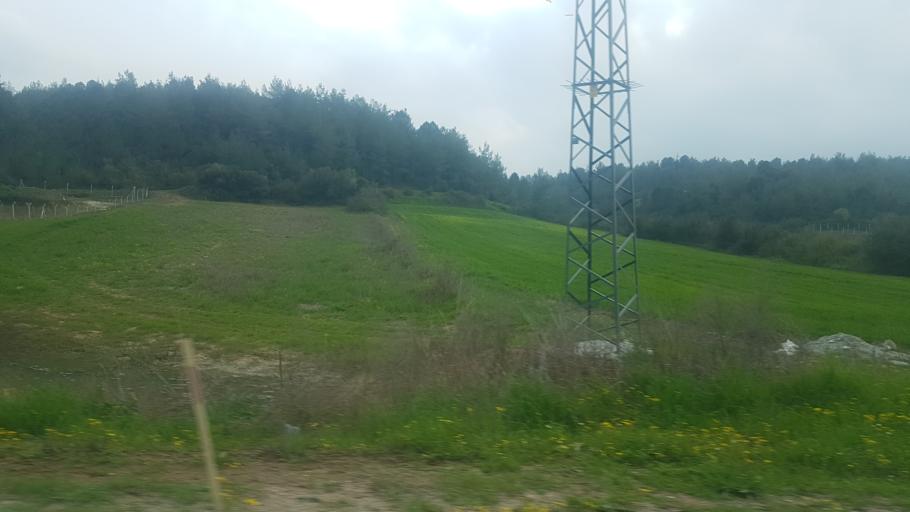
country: TR
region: Mersin
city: Yenice
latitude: 37.0907
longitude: 35.1508
